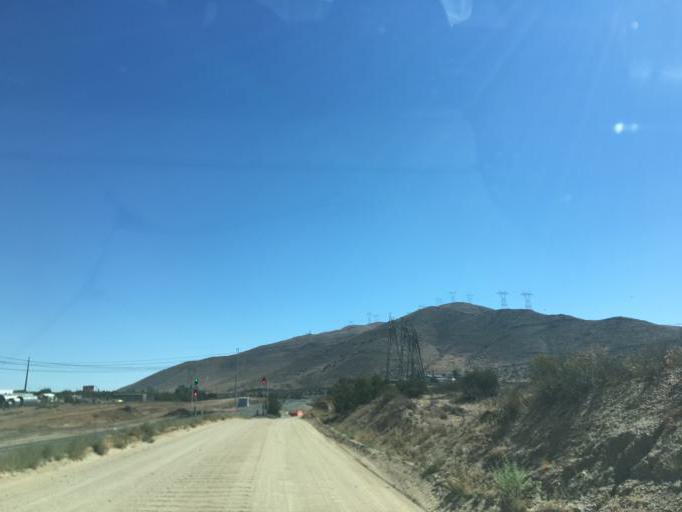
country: US
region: California
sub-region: Los Angeles County
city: Vincent
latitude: 34.4935
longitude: -118.1241
